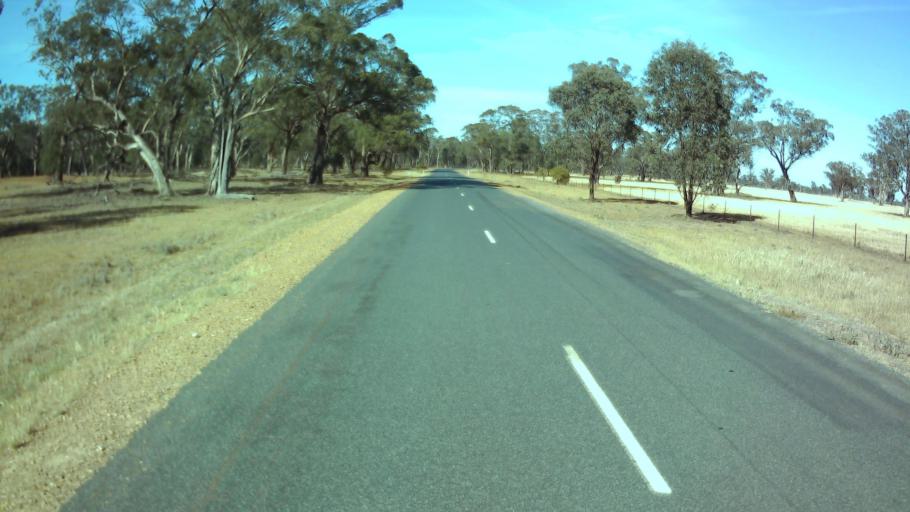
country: AU
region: New South Wales
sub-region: Weddin
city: Grenfell
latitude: -34.1326
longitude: 147.7927
